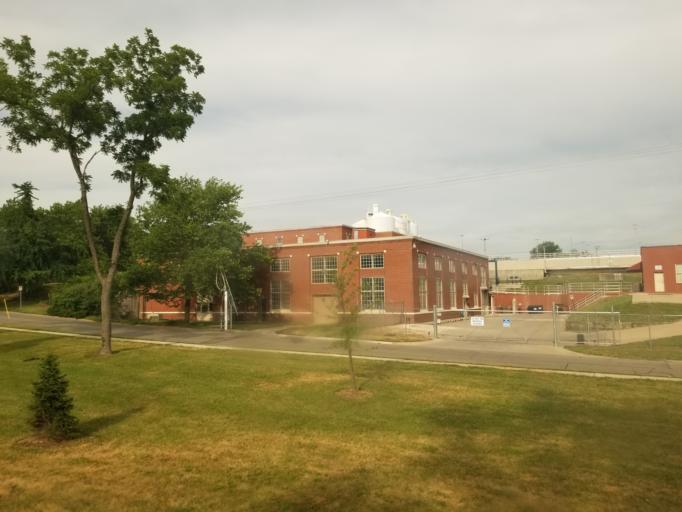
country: US
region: Kansas
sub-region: Douglas County
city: Lawrence
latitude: 38.9758
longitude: -95.2523
